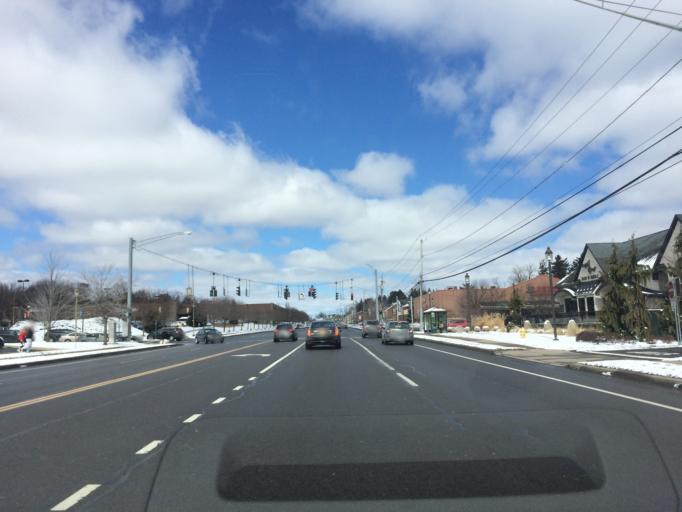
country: US
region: New York
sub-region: Monroe County
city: Pittsford
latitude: 43.1048
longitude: -77.5402
